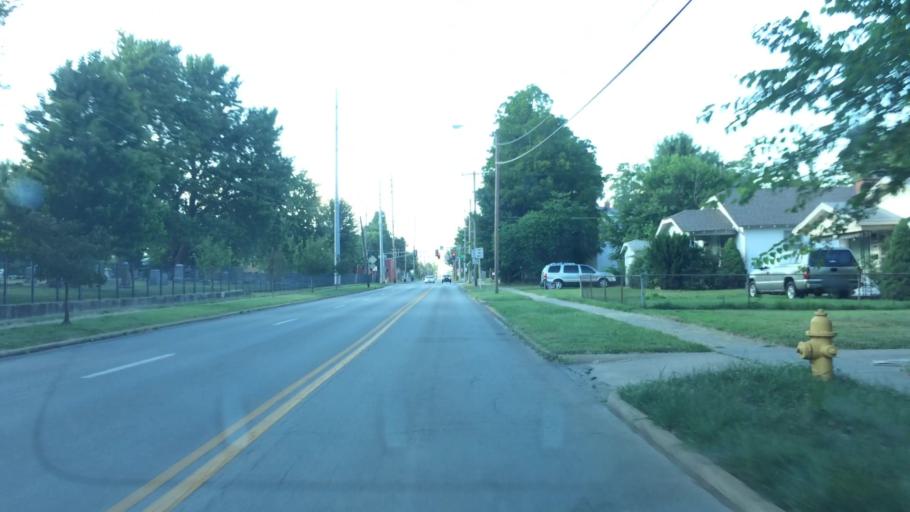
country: US
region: Missouri
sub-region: Greene County
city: Springfield
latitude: 37.1954
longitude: -93.2902
